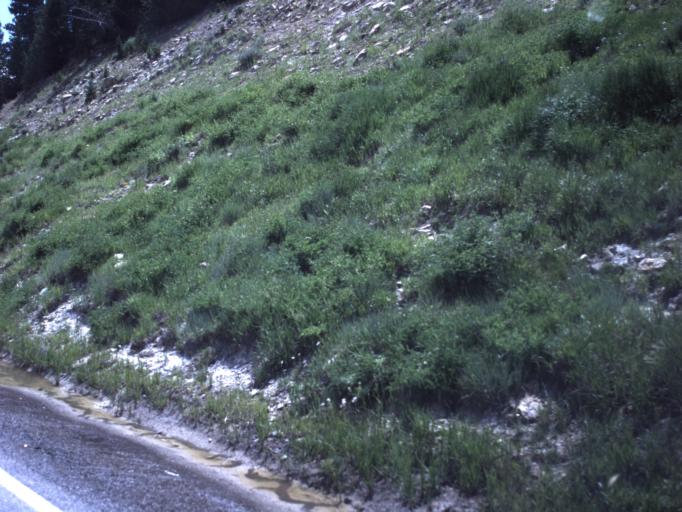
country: US
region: Utah
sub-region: Sanpete County
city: Fairview
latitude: 39.6840
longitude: -111.2469
